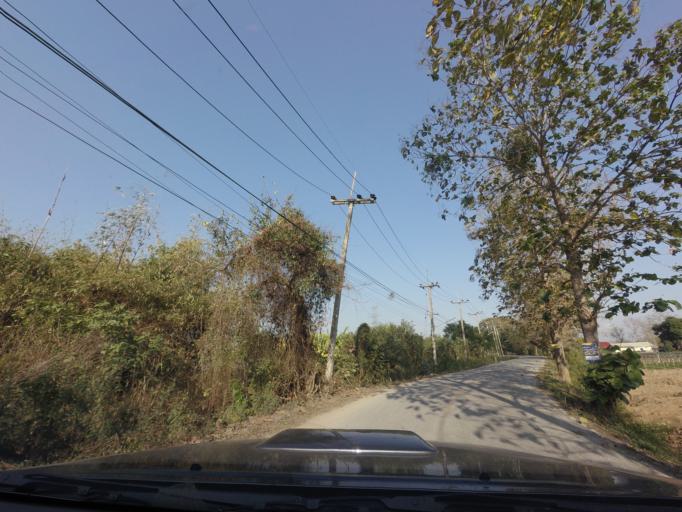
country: TH
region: Chiang Mai
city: San Sai
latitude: 18.9320
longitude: 98.9670
